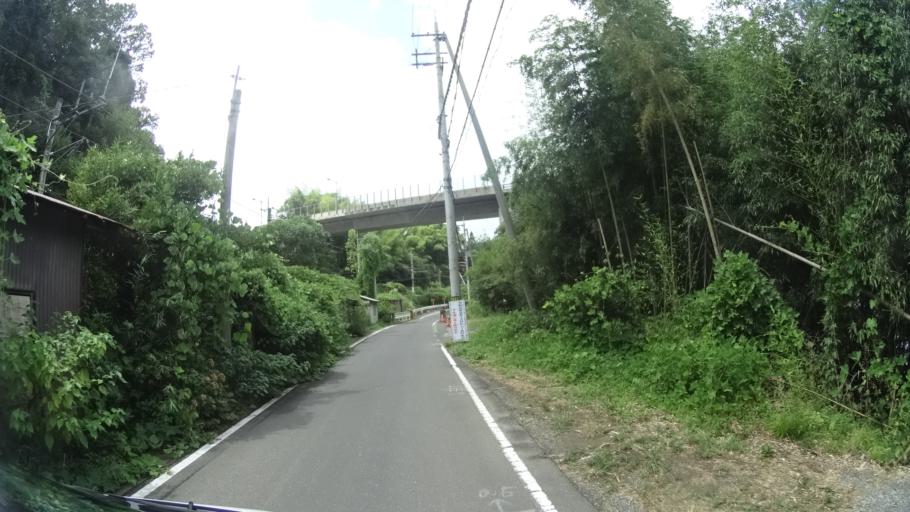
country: JP
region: Kyoto
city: Ayabe
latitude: 35.2901
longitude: 135.2670
